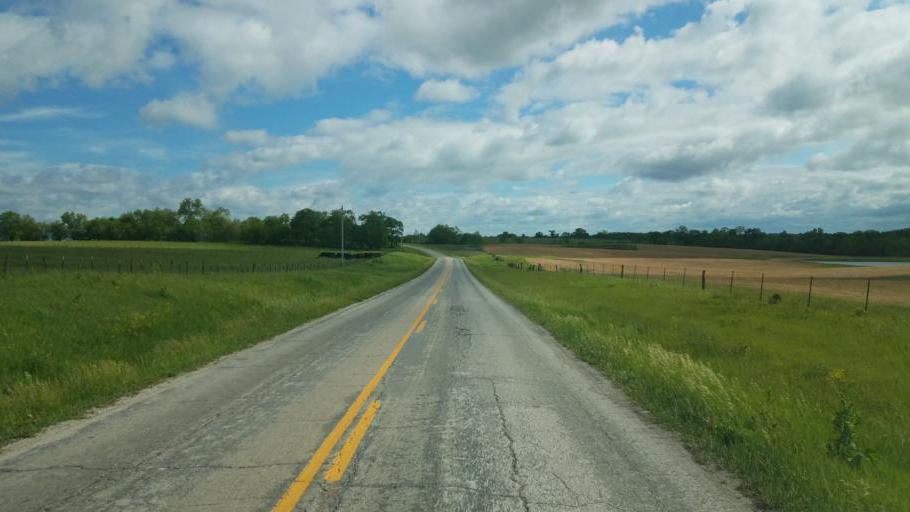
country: US
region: Missouri
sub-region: Mercer County
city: Princeton
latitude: 40.2868
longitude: -93.6803
